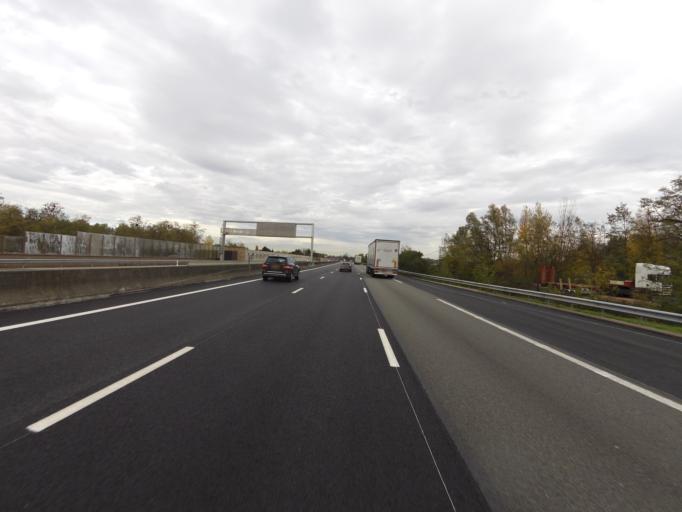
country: FR
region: Rhone-Alpes
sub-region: Departement du Rhone
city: Saint-Georges-de-Reneins
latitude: 46.0570
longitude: 4.7353
